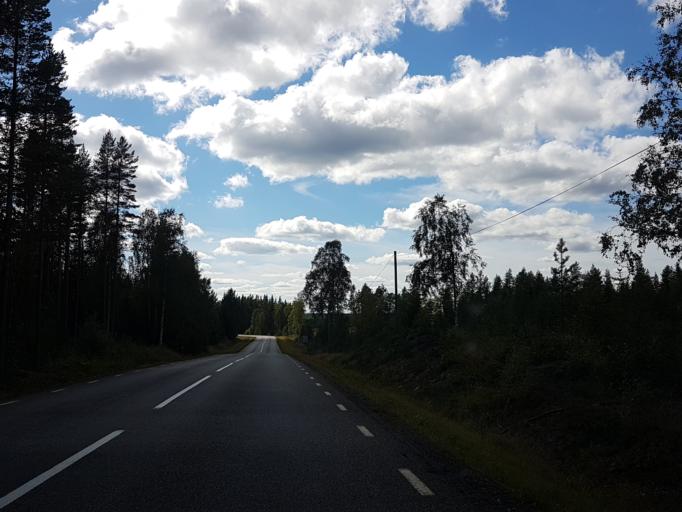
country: SE
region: Vaesterbotten
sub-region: Umea Kommun
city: Saevar
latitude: 64.1337
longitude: 20.5617
